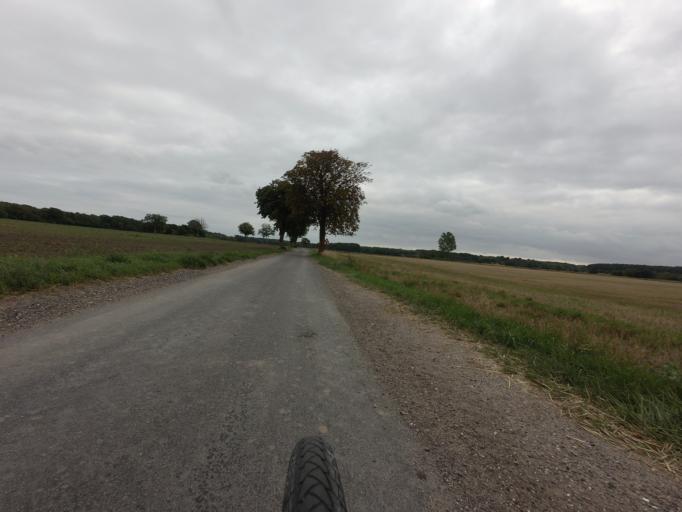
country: DK
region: Zealand
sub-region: Stevns Kommune
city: Store Heddinge
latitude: 55.3274
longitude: 12.3317
